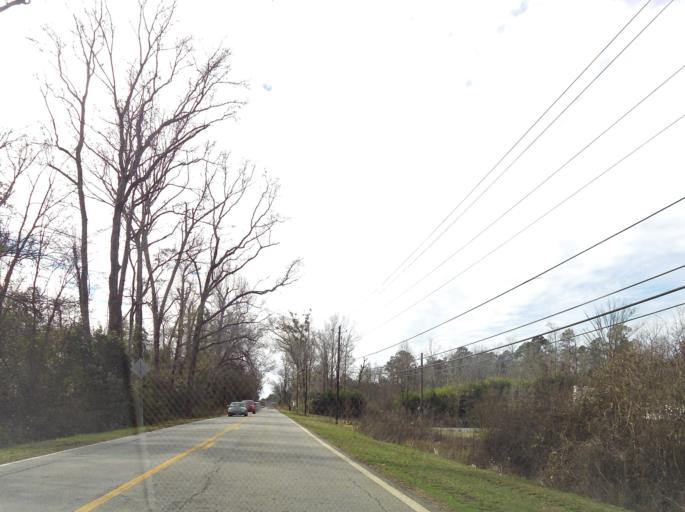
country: US
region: Georgia
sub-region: Bibb County
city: West Point
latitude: 32.8059
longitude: -83.7636
